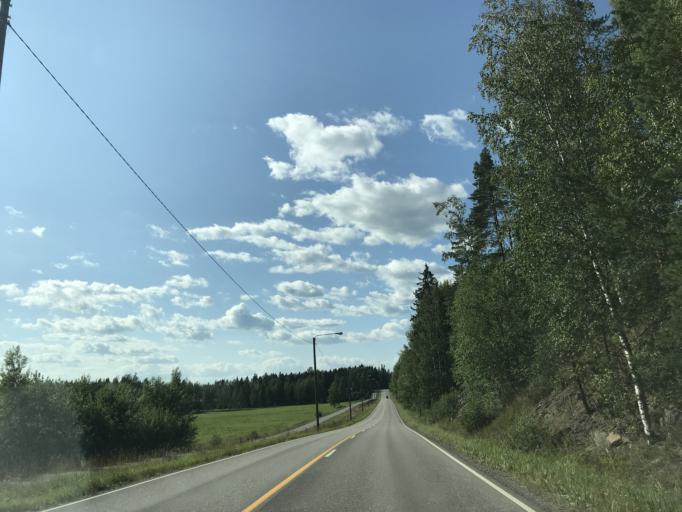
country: FI
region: Uusimaa
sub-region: Helsinki
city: Nurmijaervi
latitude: 60.4100
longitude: 24.8874
